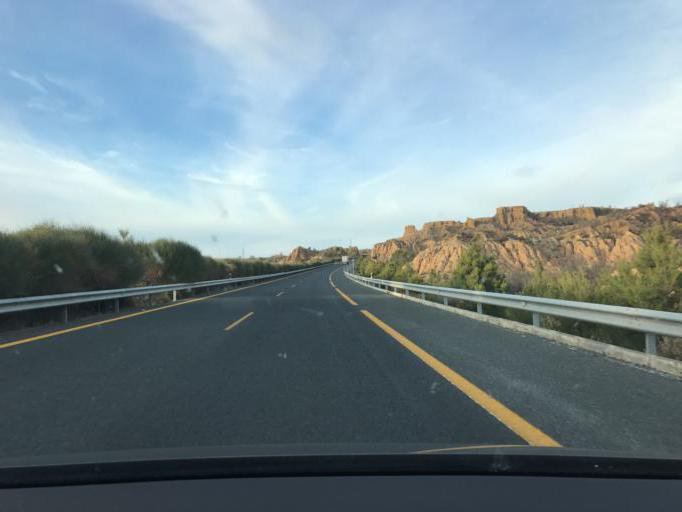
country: ES
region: Andalusia
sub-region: Provincia de Granada
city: Guadix
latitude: 37.3069
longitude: -3.1119
